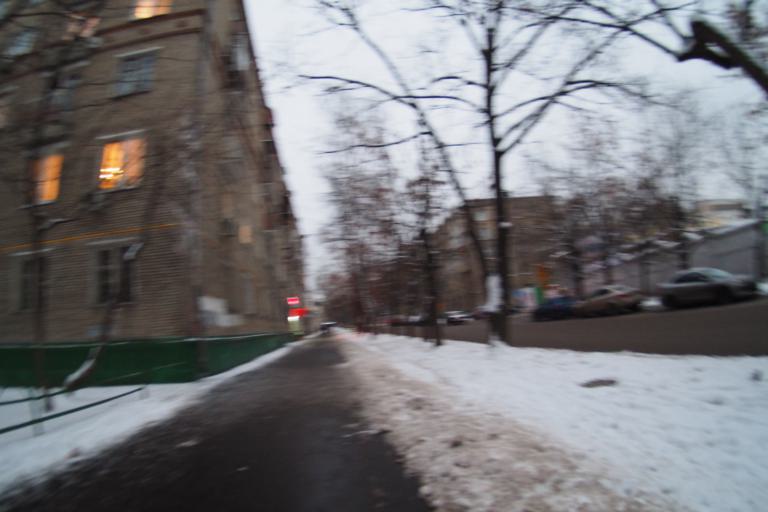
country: RU
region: Moscow
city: Sokol
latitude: 55.7985
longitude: 37.5628
